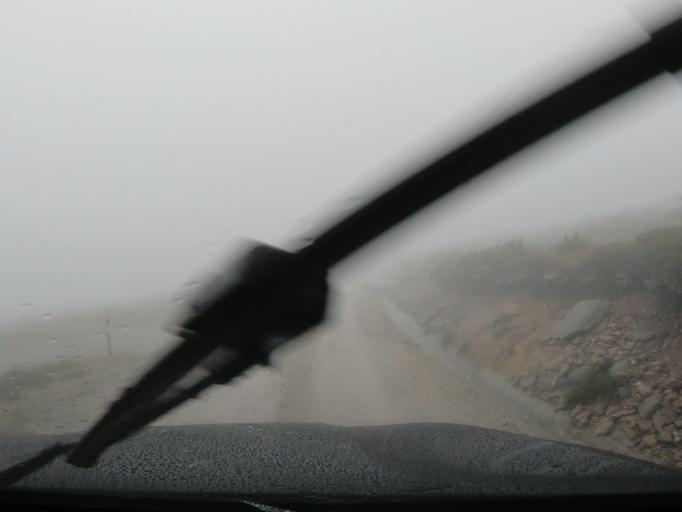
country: PT
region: Vila Real
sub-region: Vila Real
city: Vila Real
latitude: 41.3415
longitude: -7.8425
